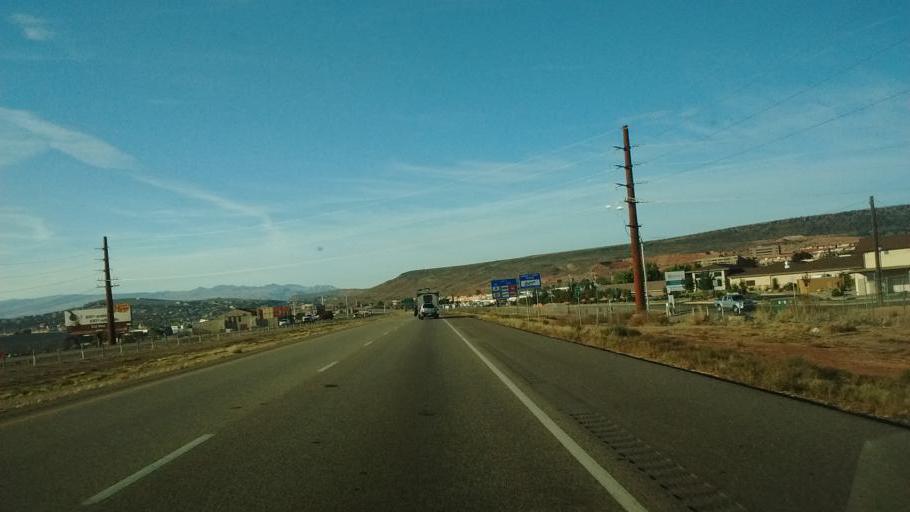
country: US
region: Utah
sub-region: Washington County
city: Saint George
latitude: 37.0911
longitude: -113.5741
